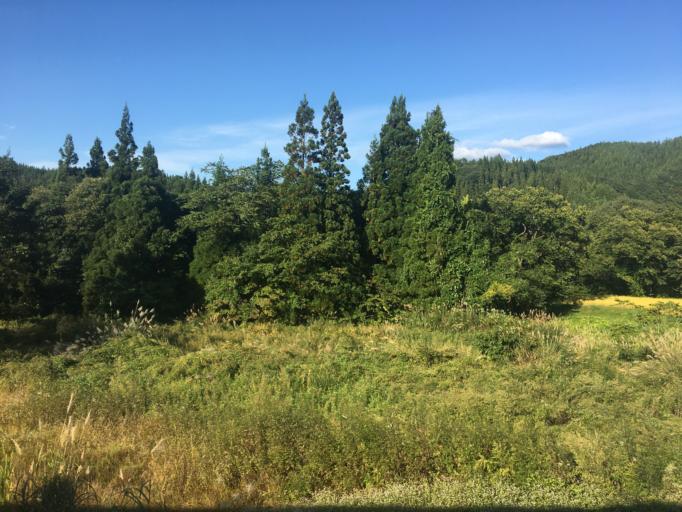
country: JP
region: Akita
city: Takanosu
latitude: 39.9071
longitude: 140.4496
